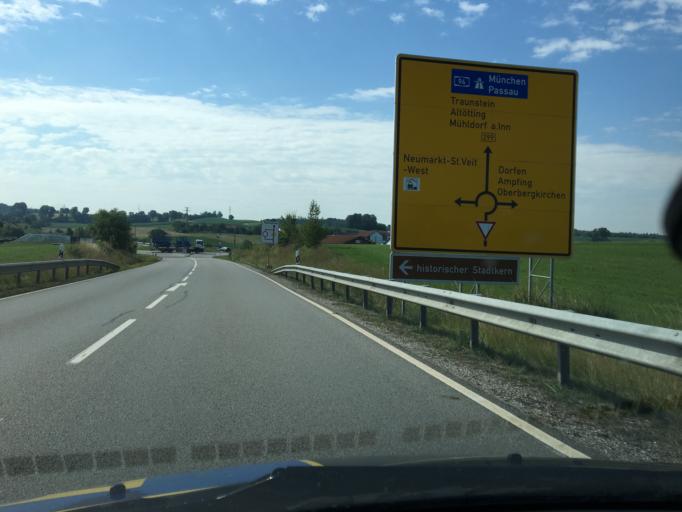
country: DE
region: Bavaria
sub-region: Upper Bavaria
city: Neumarkt-Sankt Veit
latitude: 48.3534
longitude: 12.4894
